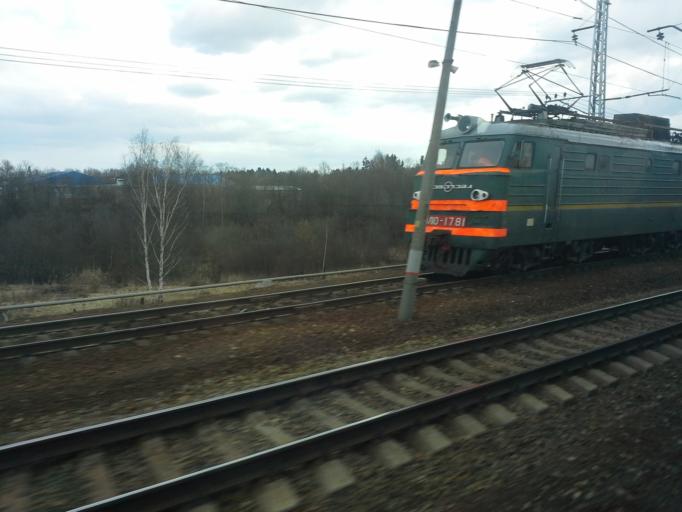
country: RU
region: Moskovskaya
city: Sofrino
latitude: 56.1327
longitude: 37.9282
